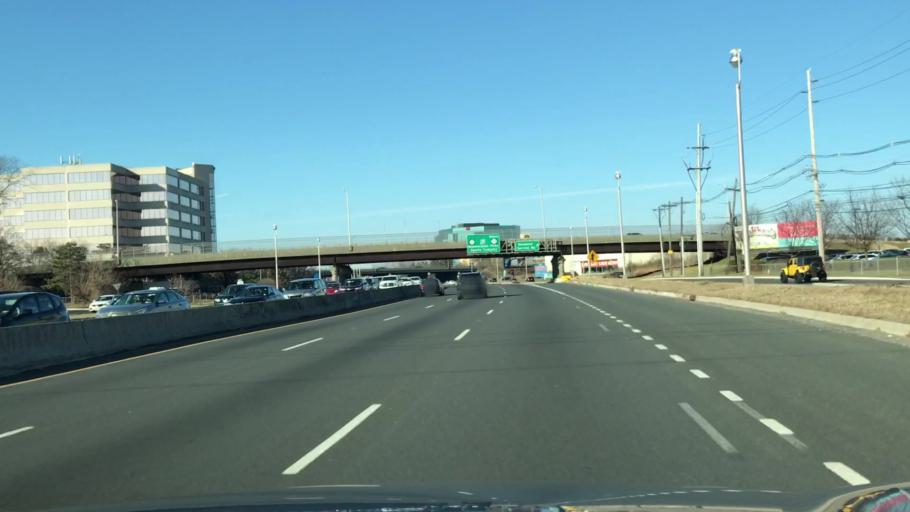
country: US
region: New Jersey
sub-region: Hudson County
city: Secaucus
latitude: 40.7844
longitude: -74.0476
